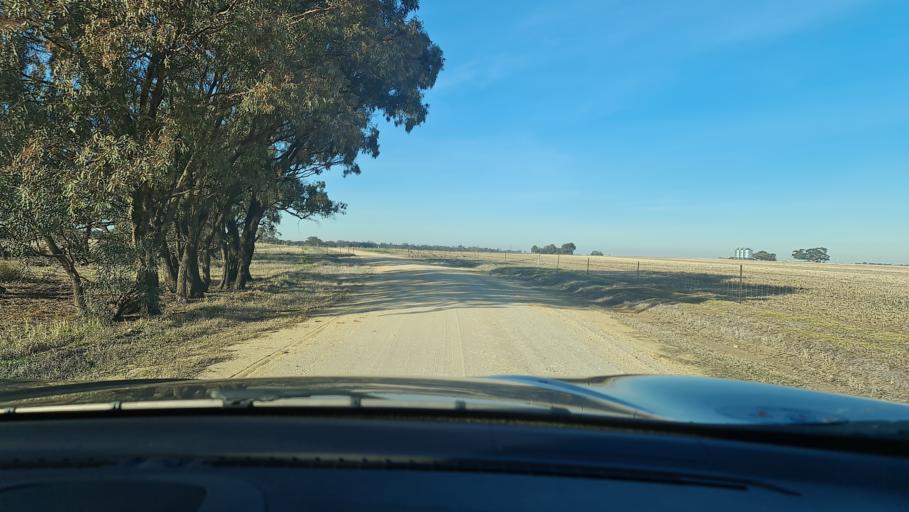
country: AU
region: Victoria
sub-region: Horsham
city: Horsham
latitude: -36.3593
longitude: 142.3963
